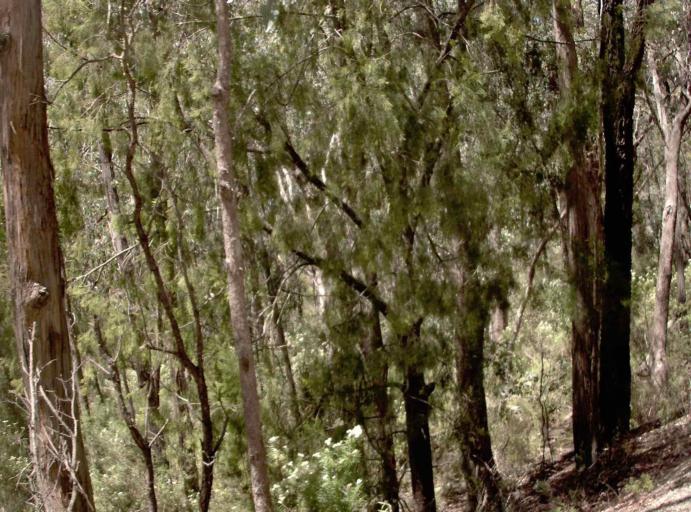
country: AU
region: Victoria
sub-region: East Gippsland
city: Lakes Entrance
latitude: -37.5798
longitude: 147.8950
